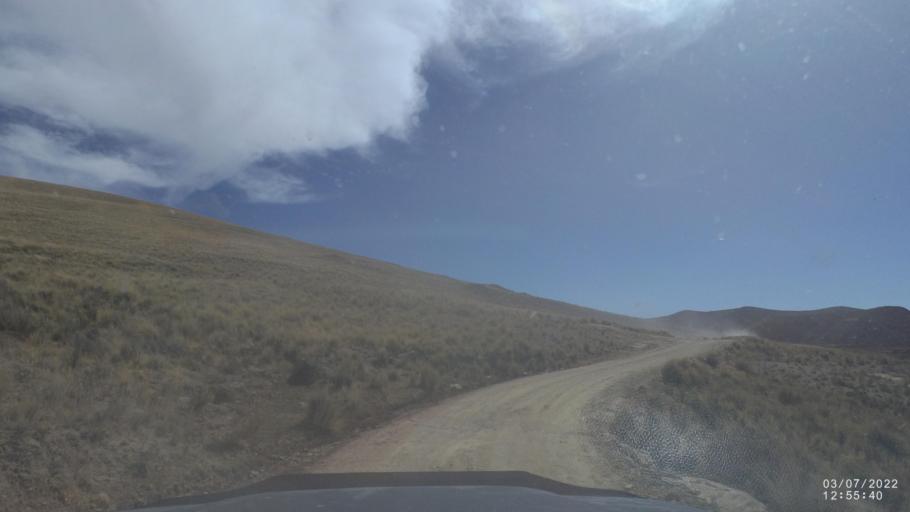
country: BO
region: Cochabamba
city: Sipe Sipe
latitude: -17.7323
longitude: -66.6709
